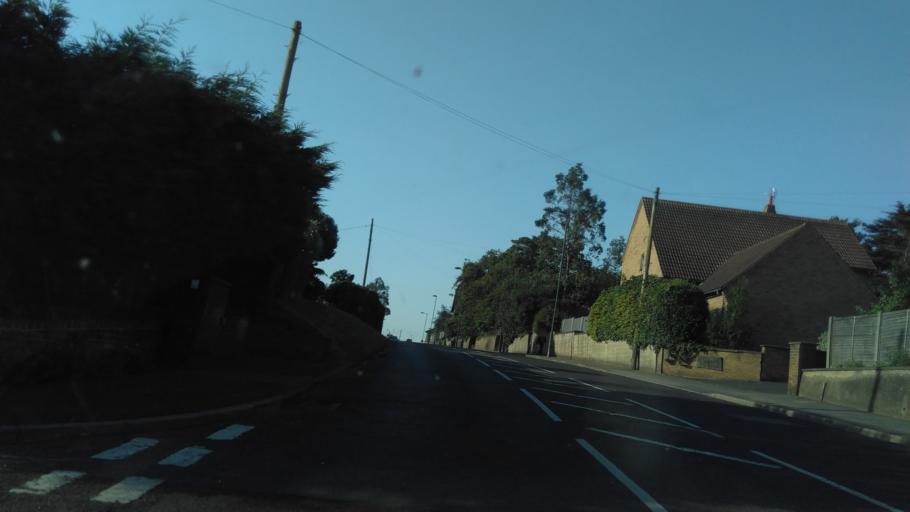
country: GB
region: England
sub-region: Kent
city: Whitstable
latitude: 51.3464
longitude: 1.0213
